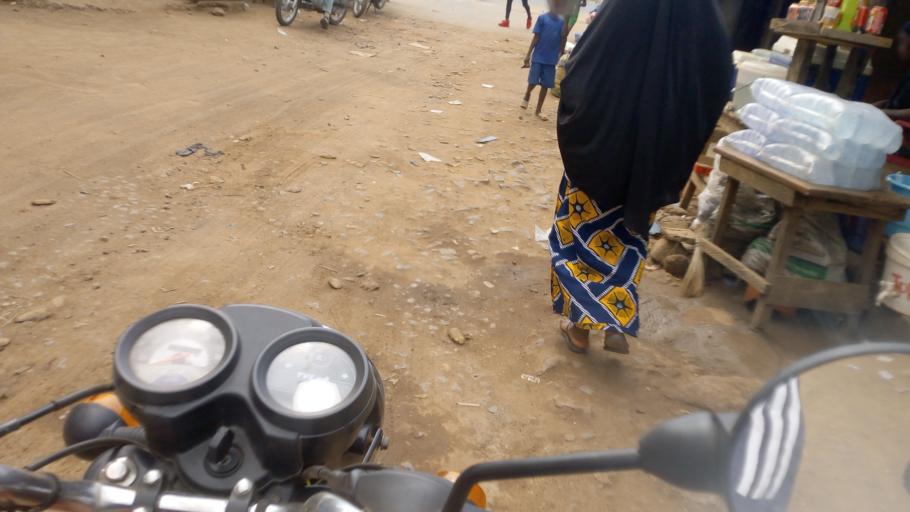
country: SL
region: Western Area
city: Waterloo
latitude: 8.3275
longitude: -13.0577
